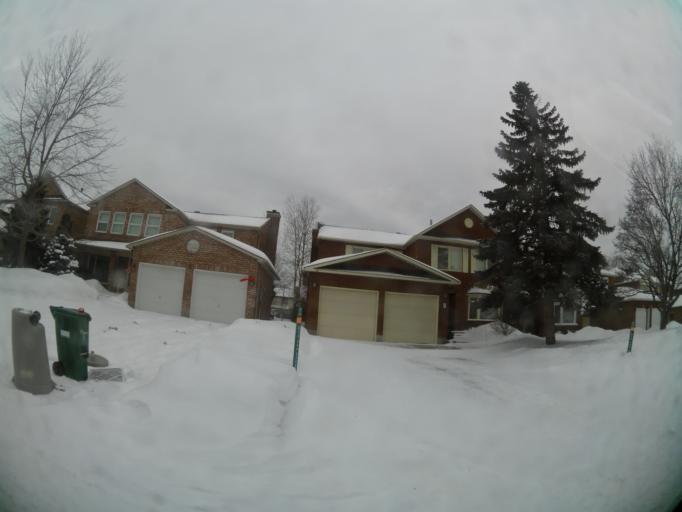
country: CA
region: Ontario
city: Ottawa
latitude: 45.3728
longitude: -75.6137
